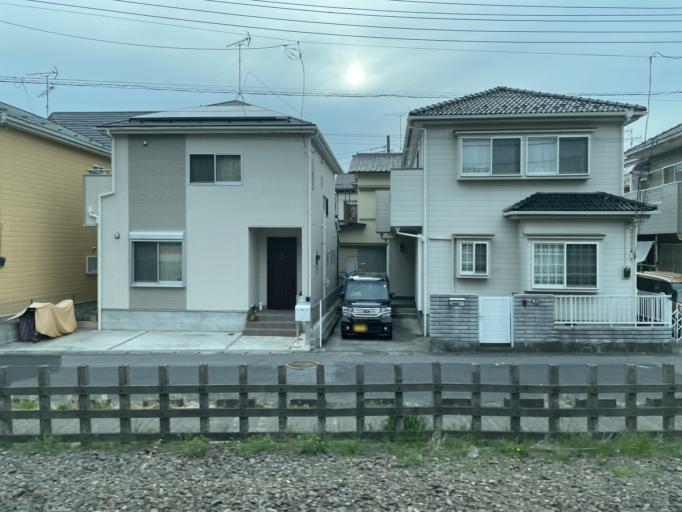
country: JP
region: Saitama
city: Kasukabe
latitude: 35.9690
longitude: 139.7647
